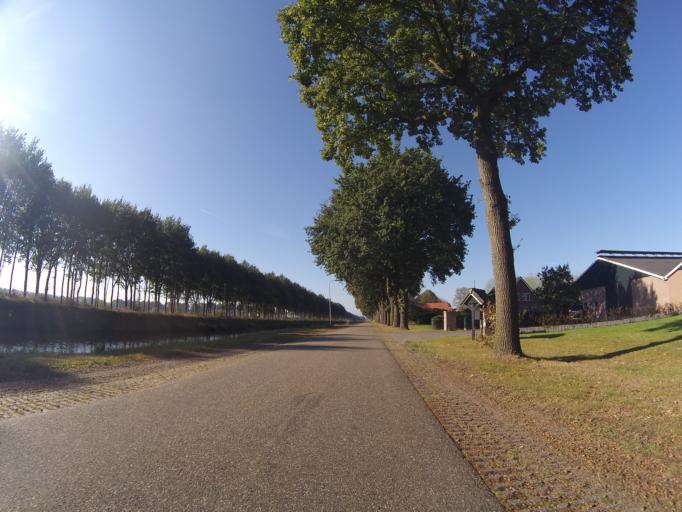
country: NL
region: Drenthe
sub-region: Gemeente Coevorden
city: Dalen
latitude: 52.7425
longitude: 6.7548
